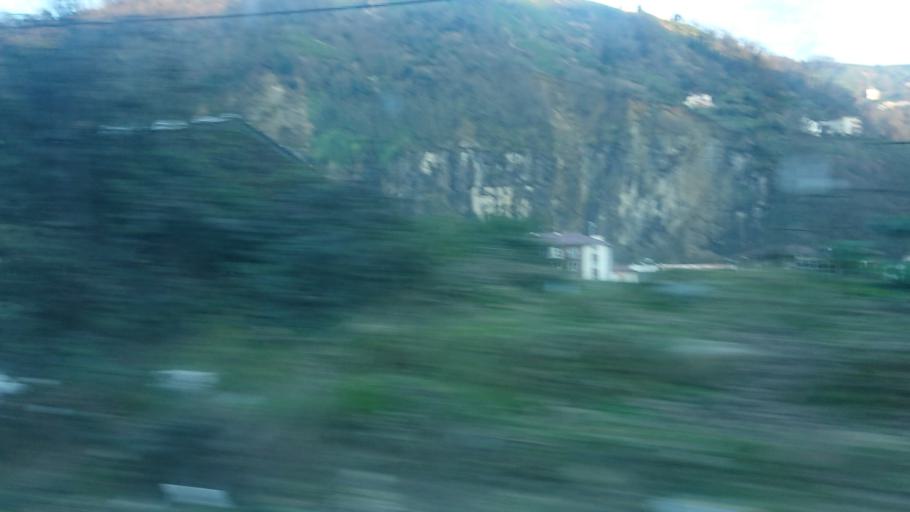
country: TR
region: Rize
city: Gundogdu
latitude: 41.0281
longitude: 40.5813
